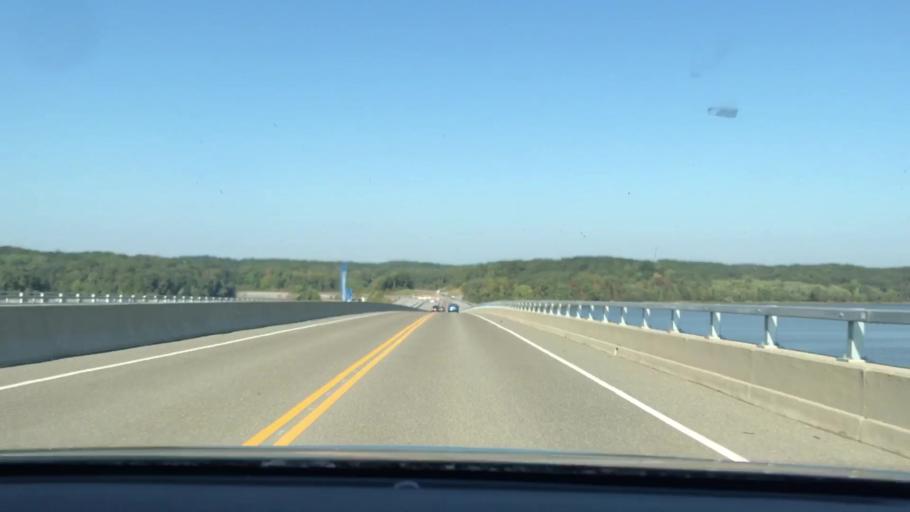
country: US
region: Kentucky
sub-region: Trigg County
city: Cadiz
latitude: 36.8001
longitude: -87.9770
